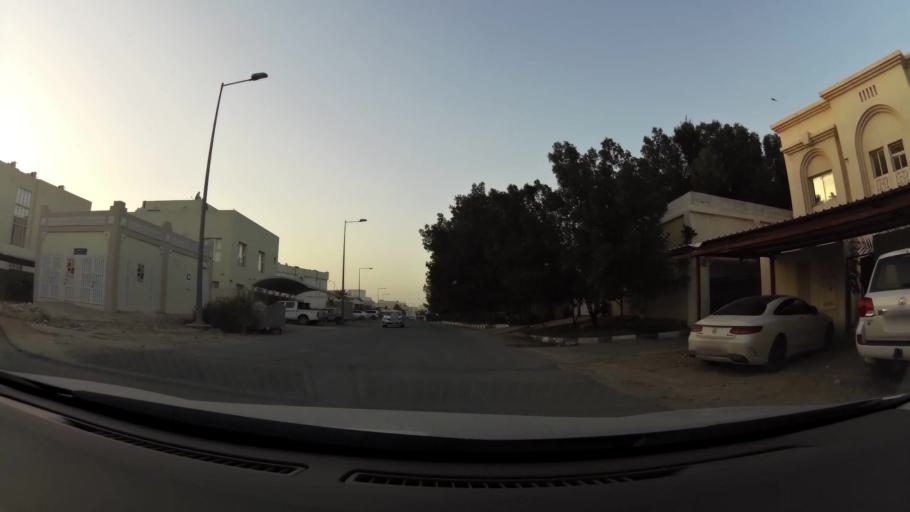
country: QA
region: Baladiyat ar Rayyan
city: Ar Rayyan
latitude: 25.3230
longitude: 51.4646
